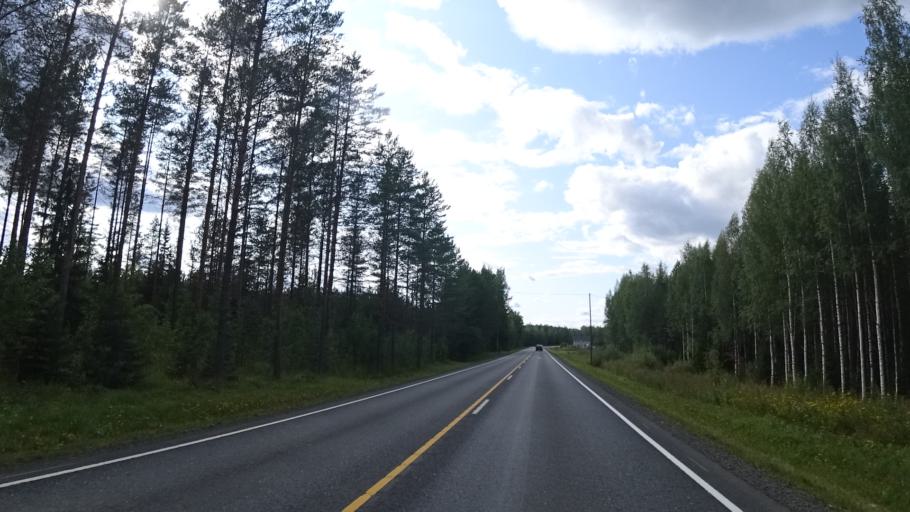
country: FI
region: North Karelia
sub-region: Keski-Karjala
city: Tohmajaervi
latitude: 62.1844
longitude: 30.4791
